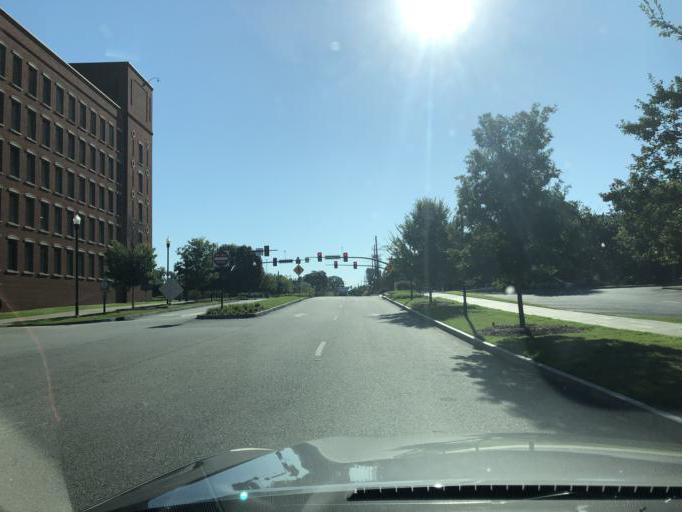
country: US
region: Alabama
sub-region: Russell County
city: Phenix City
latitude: 32.4724
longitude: -84.9942
